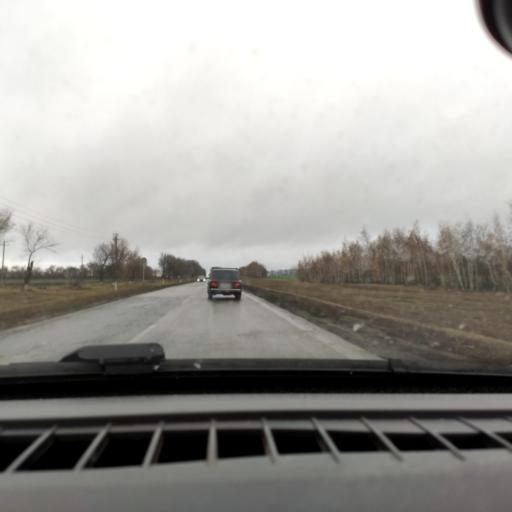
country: RU
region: Belgorod
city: Ilovka
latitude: 50.7114
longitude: 38.6583
